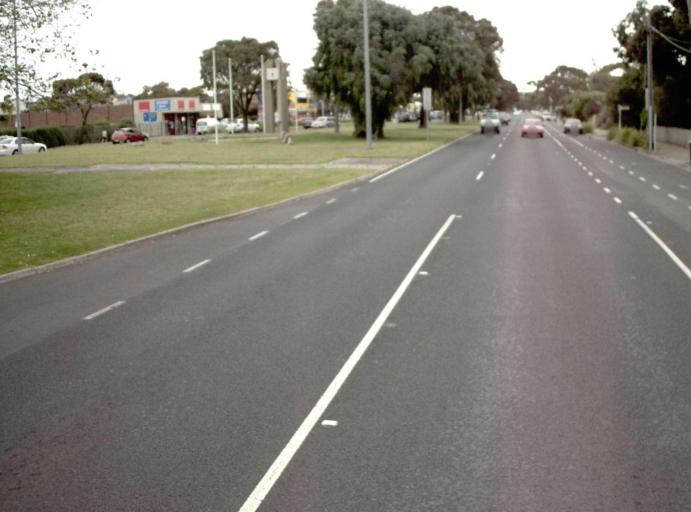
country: AU
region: Victoria
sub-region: Mornington Peninsula
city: Rosebud
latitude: -38.3543
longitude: 144.9088
